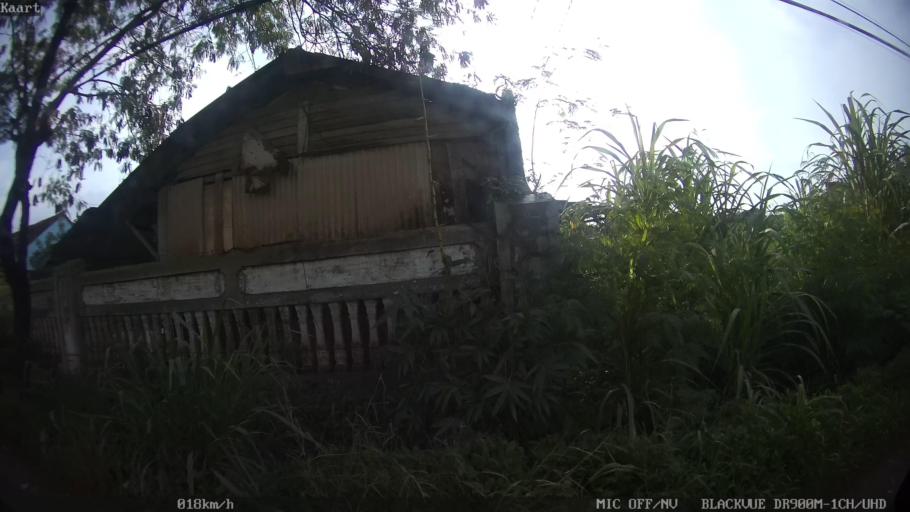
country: ID
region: Lampung
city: Kedaton
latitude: -5.3892
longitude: 105.3155
